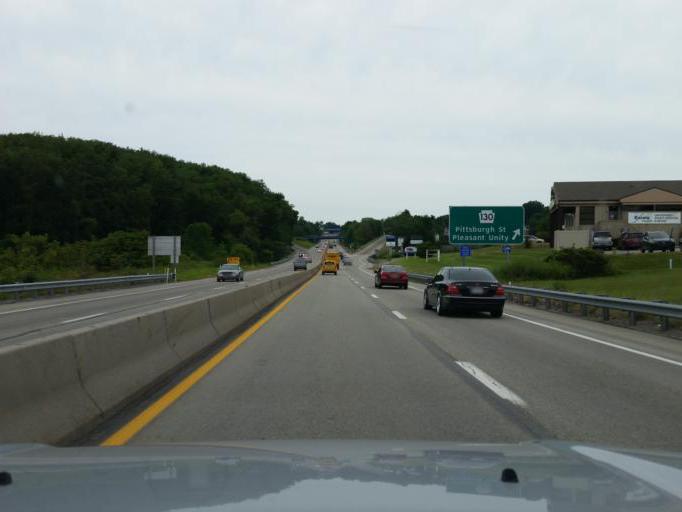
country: US
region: Pennsylvania
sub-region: Westmoreland County
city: Greensburg
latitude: 40.2920
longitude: -79.5250
